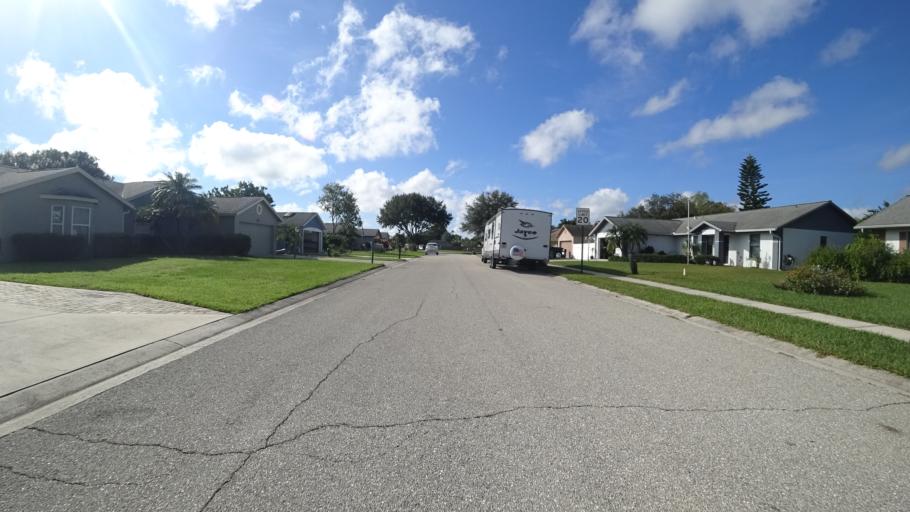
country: US
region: Florida
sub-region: Manatee County
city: Ellenton
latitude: 27.5720
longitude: -82.4994
